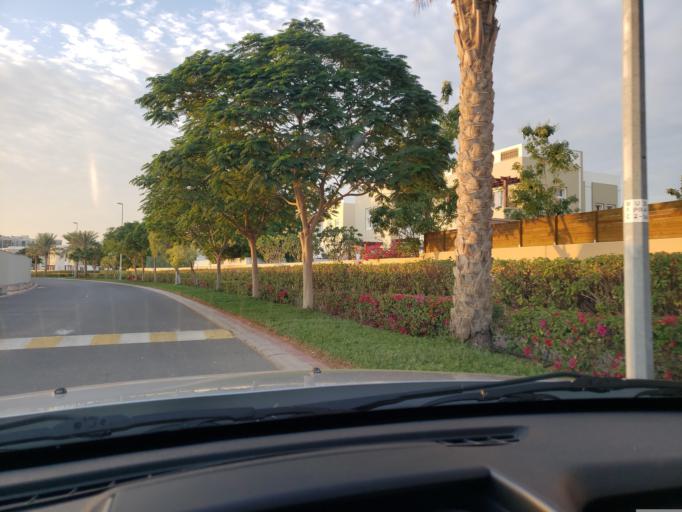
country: AE
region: Dubai
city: Dubai
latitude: 25.0216
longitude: 55.2697
